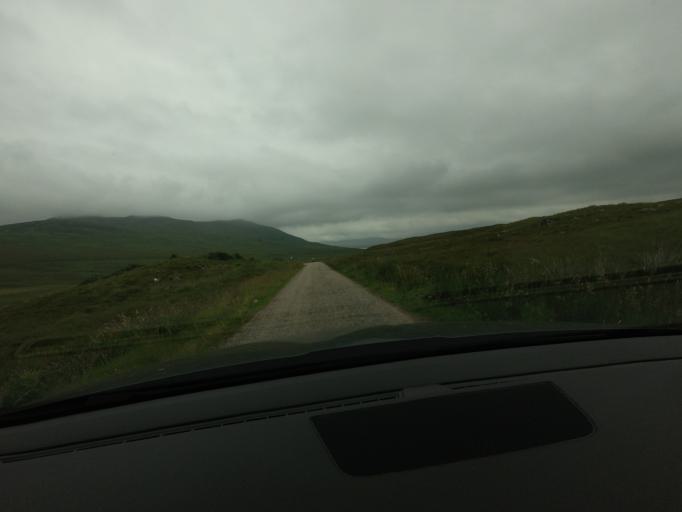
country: GB
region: Scotland
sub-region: Highland
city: Golspie
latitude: 58.3590
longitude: -4.4058
